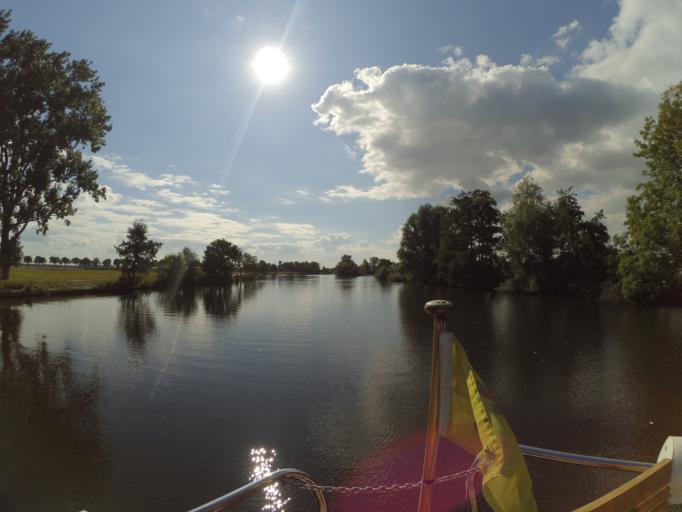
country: NL
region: Utrecht
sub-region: Stichtse Vecht
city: Vreeland
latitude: 52.2468
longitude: 5.0463
